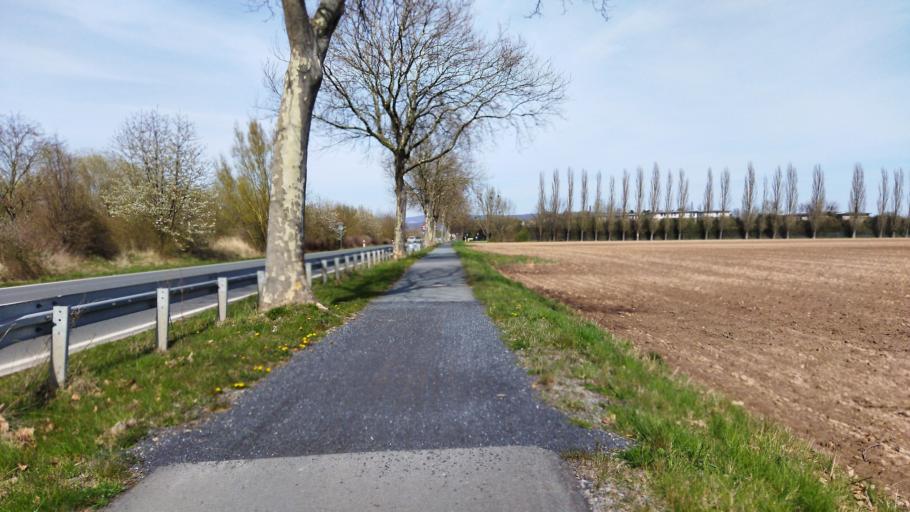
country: DE
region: Lower Saxony
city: Hameln
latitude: 52.0748
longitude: 9.3780
